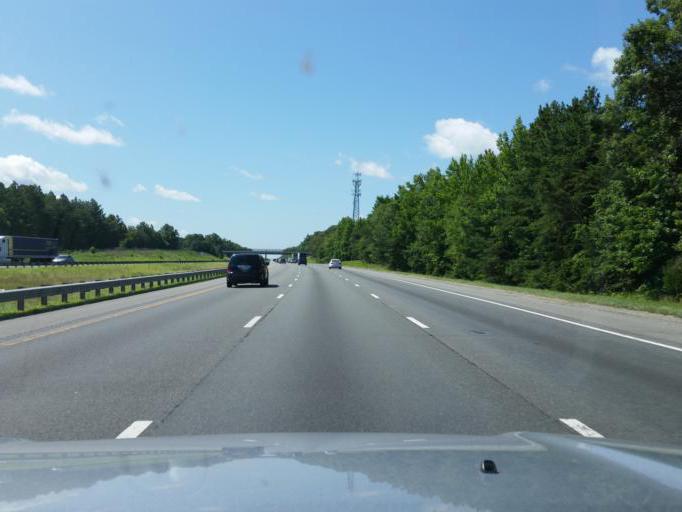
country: US
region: Virginia
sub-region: Spotsylvania County
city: Spotsylvania Courthouse
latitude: 38.1994
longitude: -77.5003
